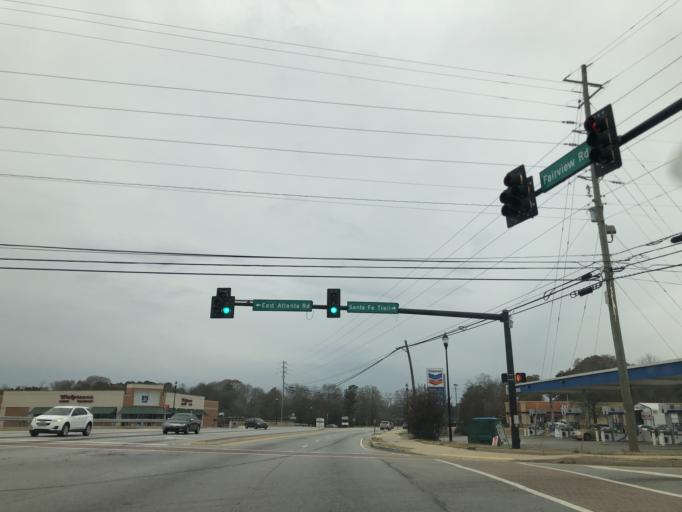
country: US
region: Georgia
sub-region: Henry County
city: Stockbridge
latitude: 33.6187
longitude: -84.2456
